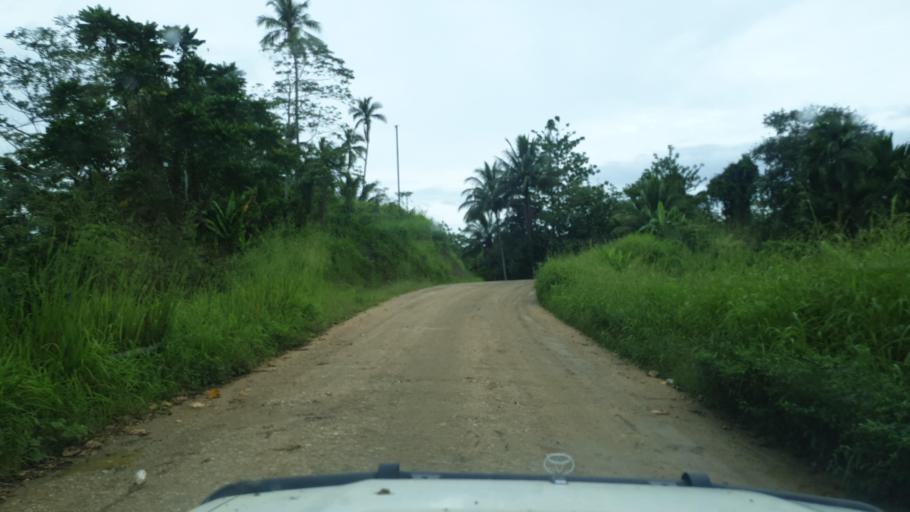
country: PG
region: Gulf
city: Kerema
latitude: -7.9838
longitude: 145.7852
